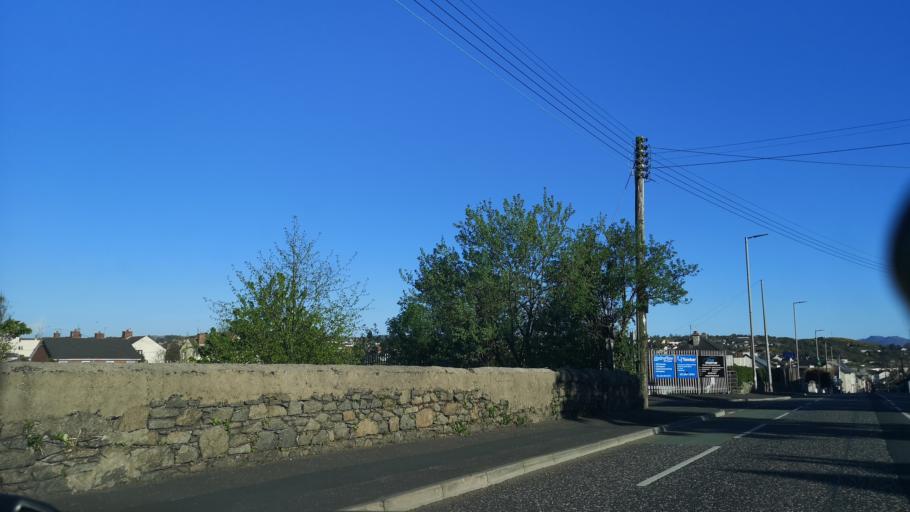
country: GB
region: Northern Ireland
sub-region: Newry and Mourne District
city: Newry
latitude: 54.1838
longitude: -6.3424
